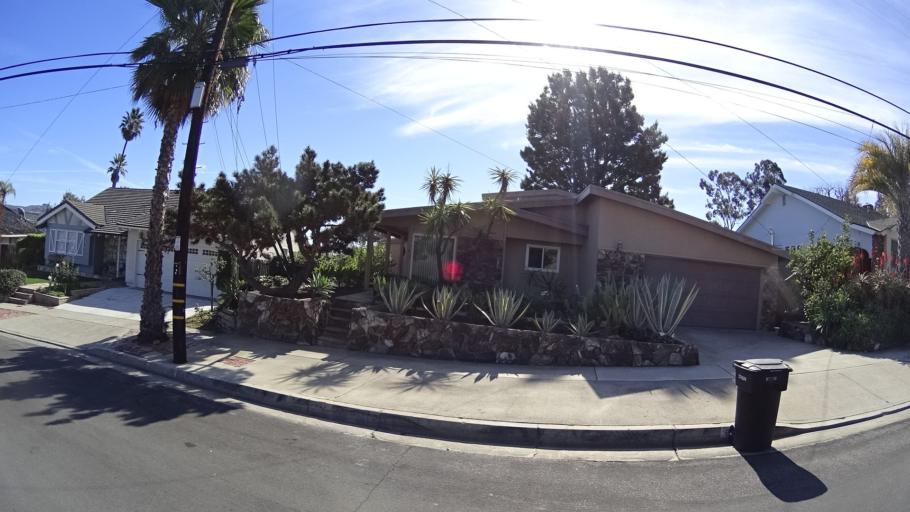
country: US
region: California
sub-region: Orange County
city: Dana Point
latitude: 33.4745
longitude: -117.6875
